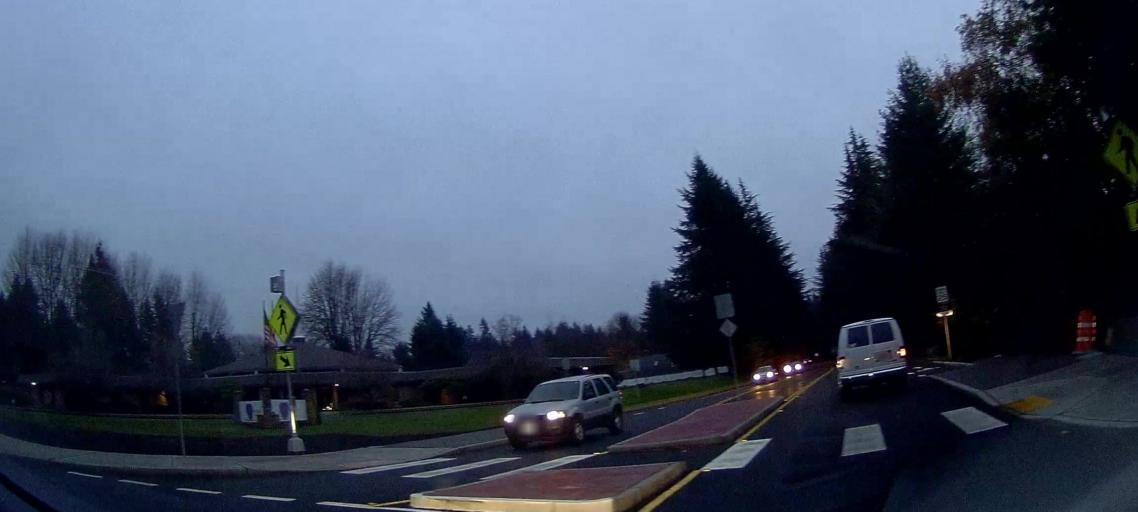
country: US
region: Washington
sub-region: Thurston County
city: Olympia
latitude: 47.0232
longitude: -122.8787
